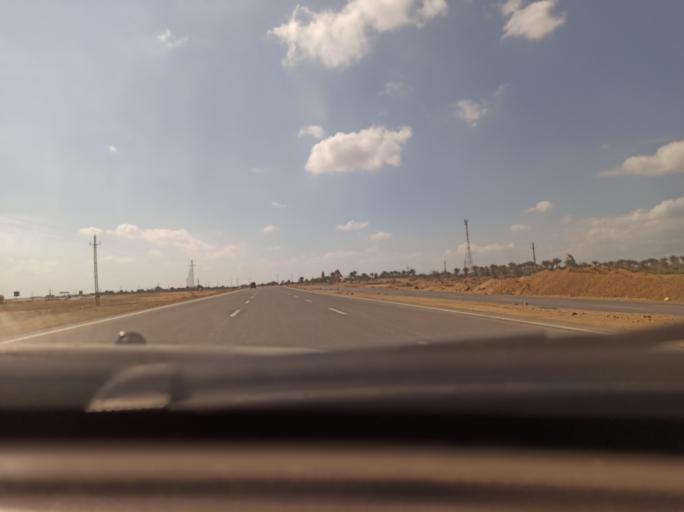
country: EG
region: Muhafazat al Fayyum
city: Al Wasitah
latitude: 29.3720
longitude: 31.0828
